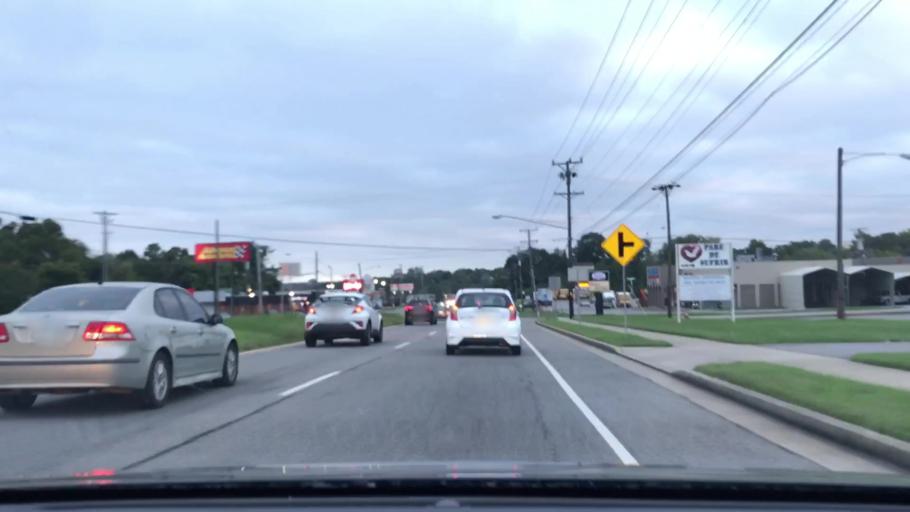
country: US
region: Tennessee
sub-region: Davidson County
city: Oak Hill
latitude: 36.0622
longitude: -86.7167
